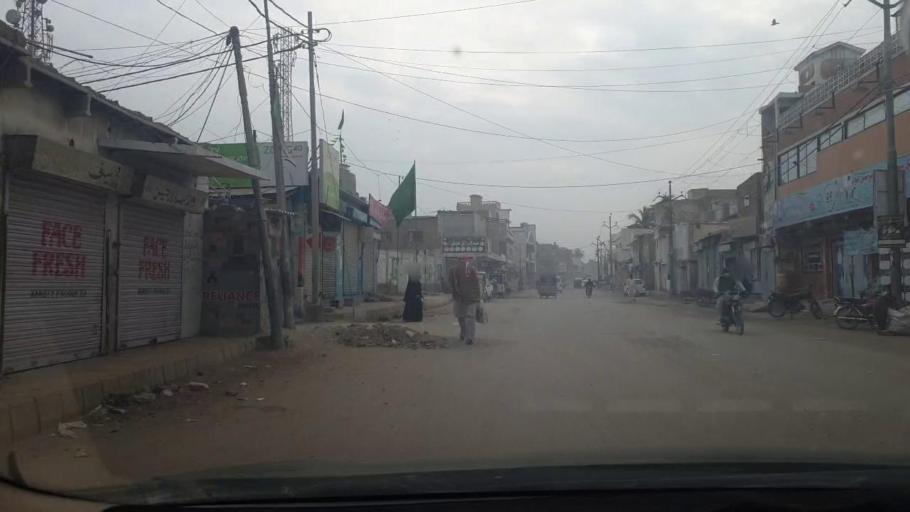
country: PK
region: Sindh
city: Malir Cantonment
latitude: 24.8790
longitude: 67.1926
